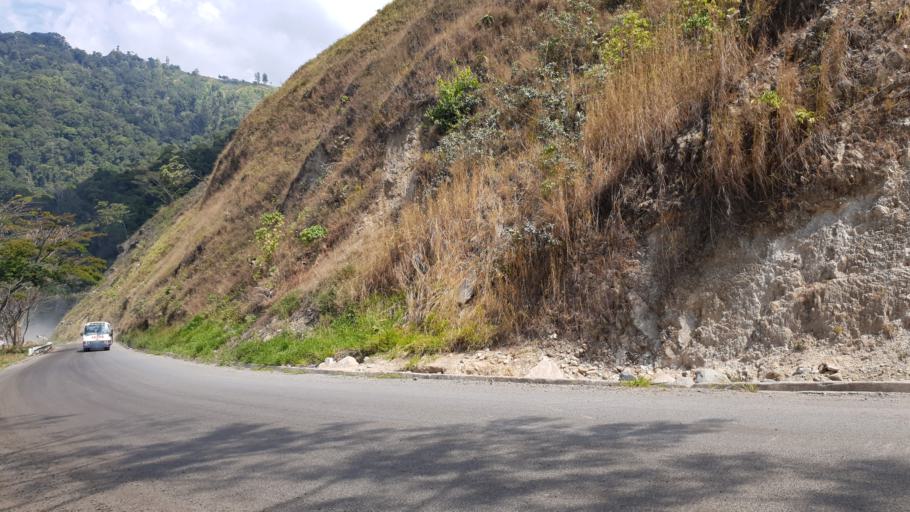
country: PG
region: Eastern Highlands
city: Kainantu
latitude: -6.1985
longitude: 146.0424
